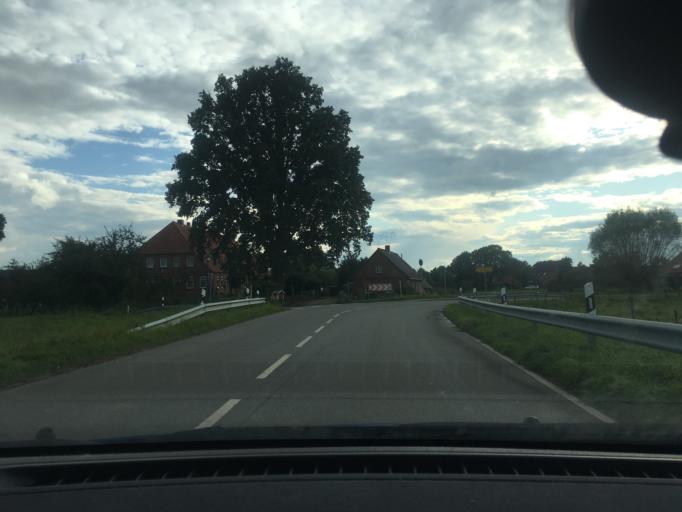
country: DE
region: Lower Saxony
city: Neu Darchau
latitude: 53.2405
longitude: 10.8981
